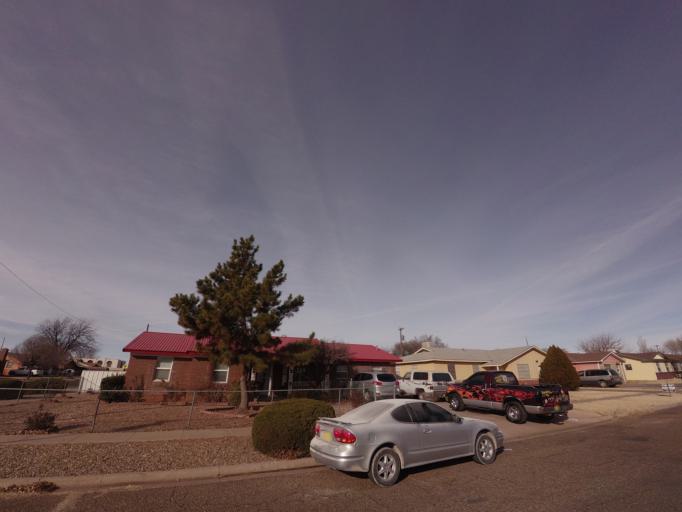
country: US
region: New Mexico
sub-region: Curry County
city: Clovis
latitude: 34.4138
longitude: -103.2210
